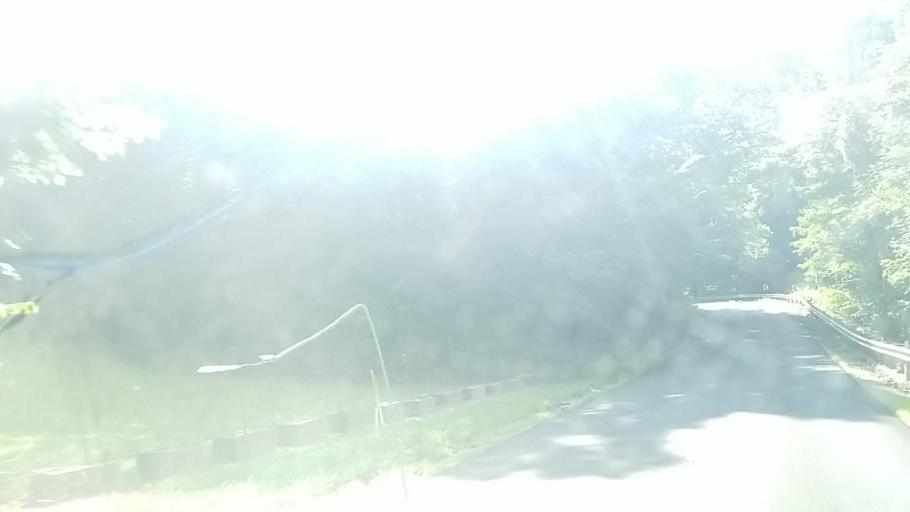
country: US
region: Ohio
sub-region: Richland County
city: Lincoln Heights
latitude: 40.6910
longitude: -82.3918
